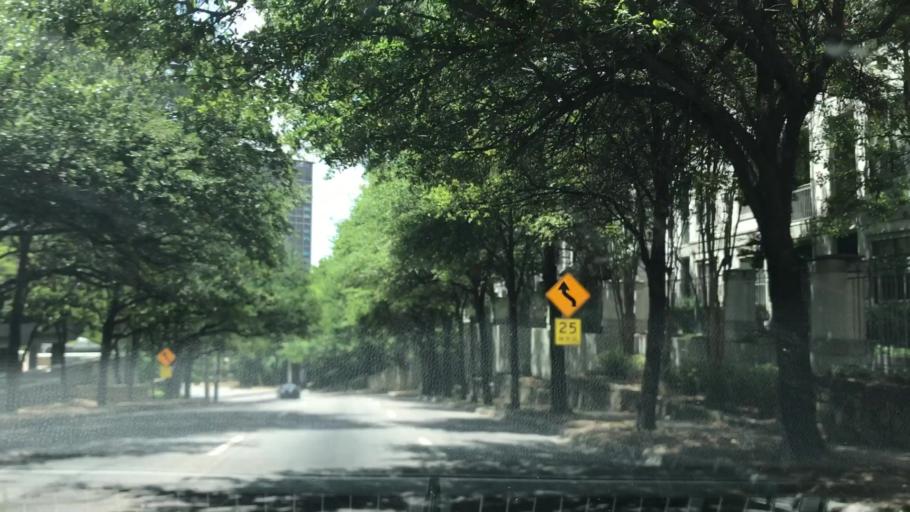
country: US
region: Texas
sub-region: Dallas County
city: Highland Park
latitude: 32.8088
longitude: -96.7999
